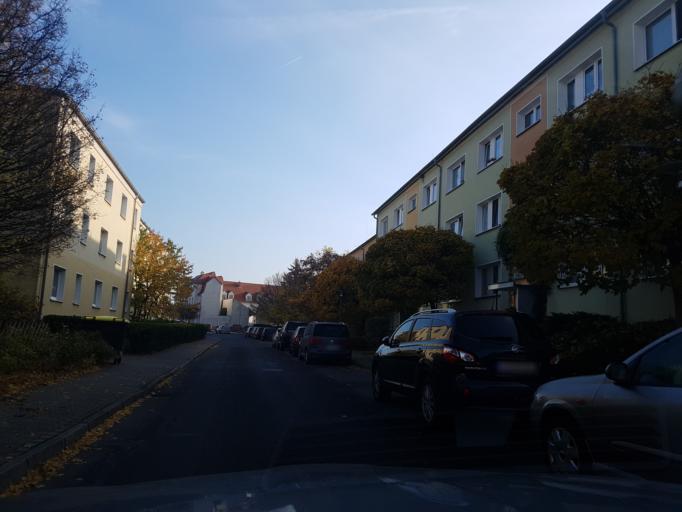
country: DE
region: Brandenburg
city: Elsterwerda
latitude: 51.4576
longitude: 13.5205
